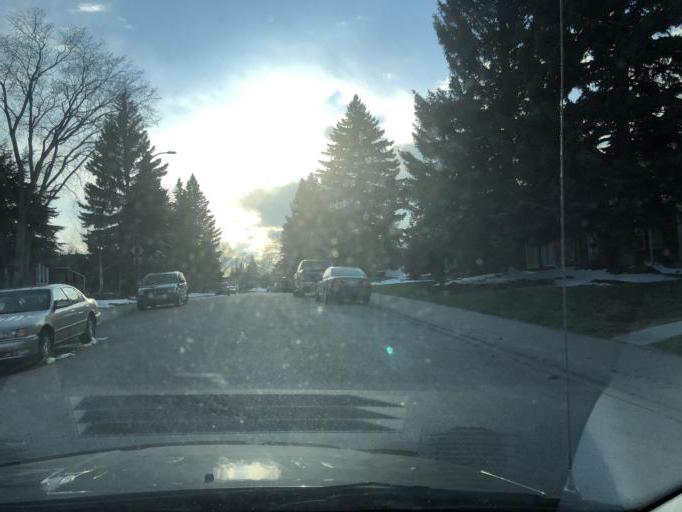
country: CA
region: Alberta
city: Calgary
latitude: 50.9419
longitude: -114.0366
